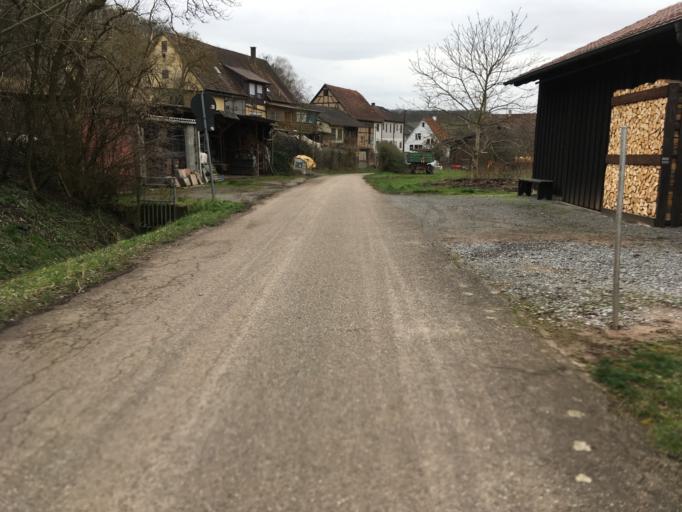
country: DE
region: Baden-Wuerttemberg
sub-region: Regierungsbezirk Stuttgart
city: Brackenheim
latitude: 49.1076
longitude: 9.0537
